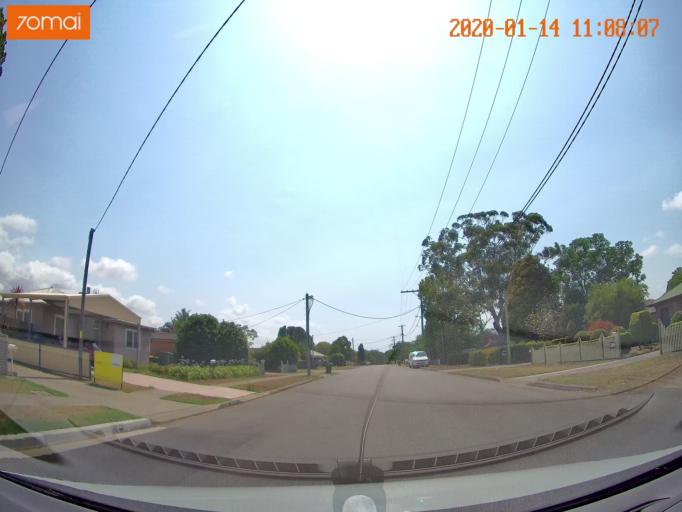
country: AU
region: New South Wales
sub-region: Lake Macquarie Shire
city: Dora Creek
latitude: -33.0967
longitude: 151.4736
